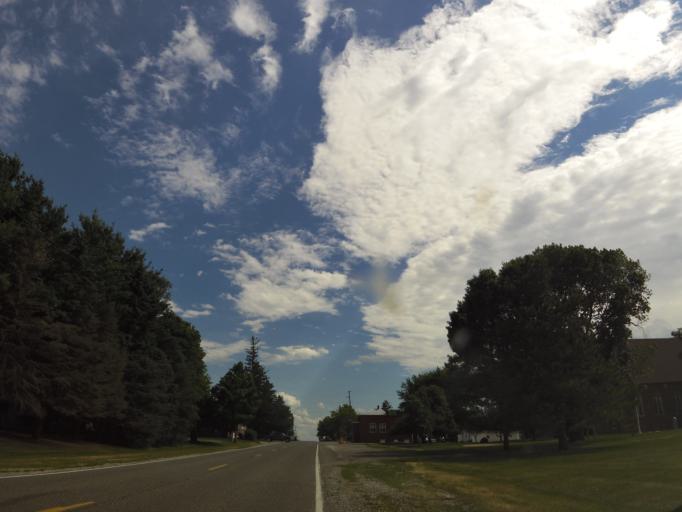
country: US
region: Iowa
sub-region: Henry County
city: Winfield
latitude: 41.1063
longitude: -91.5448
